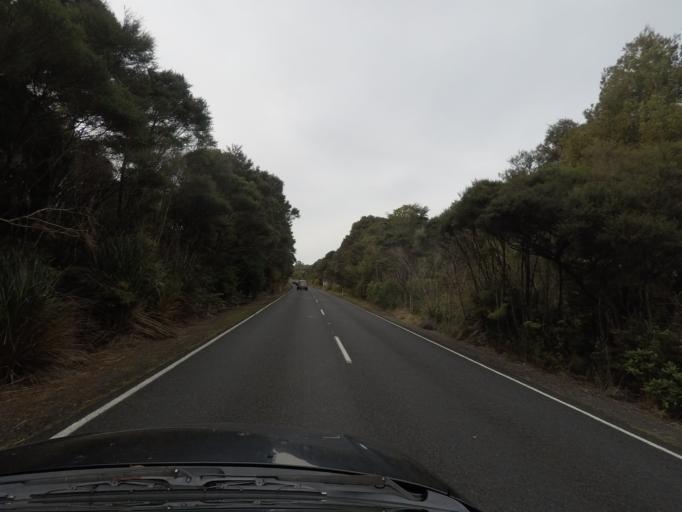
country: NZ
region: Auckland
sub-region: Auckland
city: Titirangi
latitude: -36.9360
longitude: 174.5598
